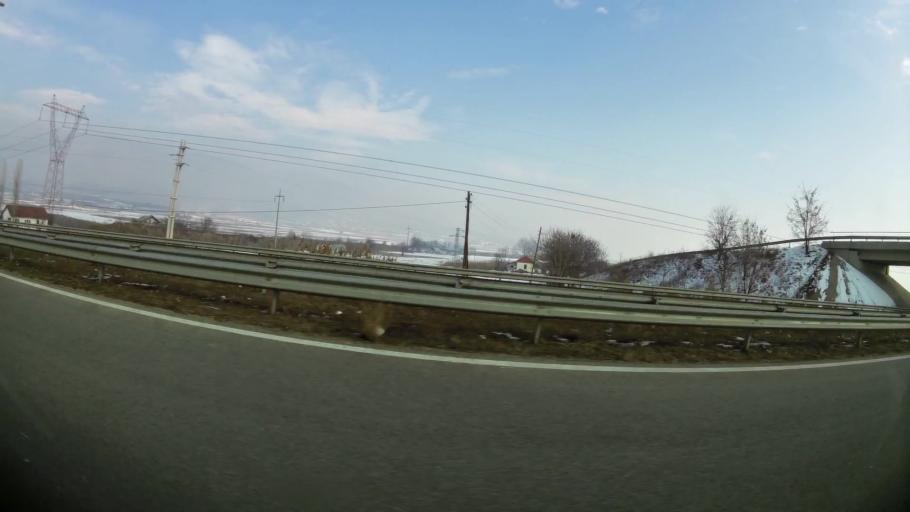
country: MK
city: Creshevo
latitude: 42.0274
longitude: 21.5301
